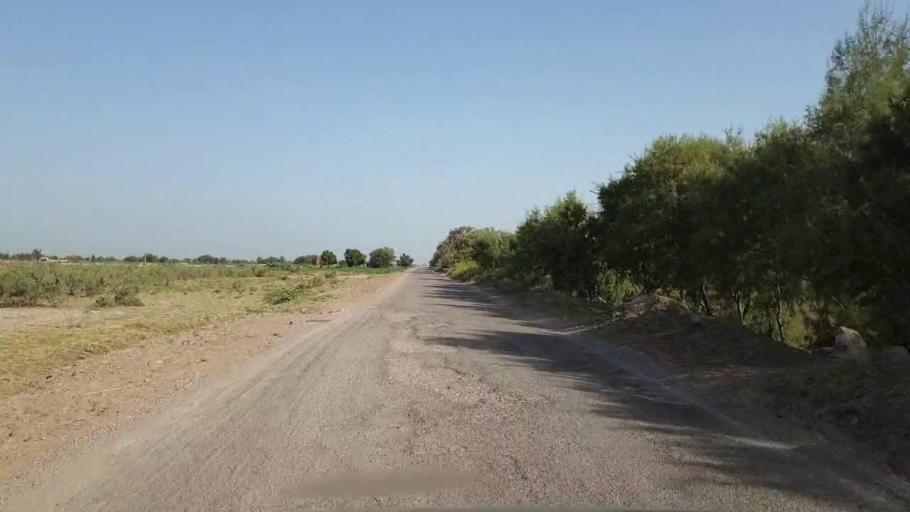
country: PK
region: Sindh
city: Nawabshah
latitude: 26.1574
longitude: 68.4452
